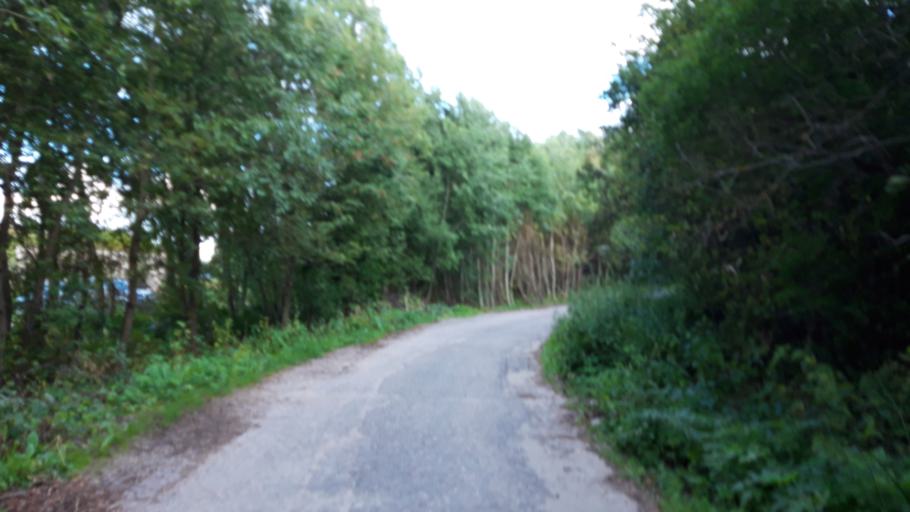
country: RU
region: Tverskaya
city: Konakovo
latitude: 56.6723
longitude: 36.7302
